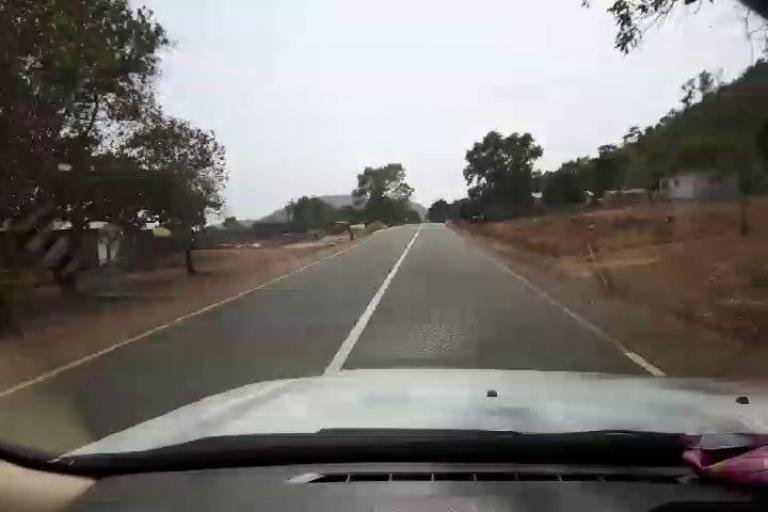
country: SL
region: Western Area
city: Waterloo
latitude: 8.2021
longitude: -13.1199
